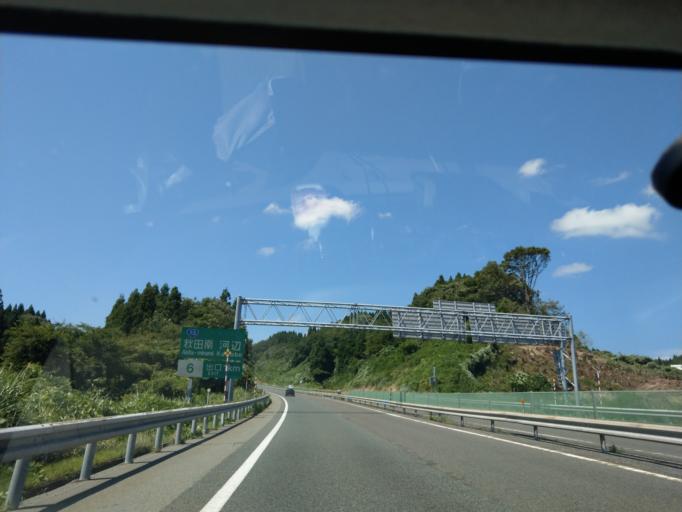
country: JP
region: Akita
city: Akita
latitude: 39.6525
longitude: 140.2043
